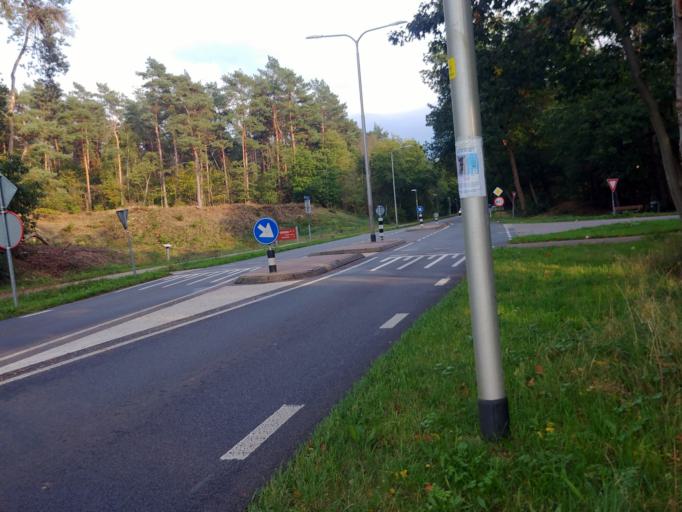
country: NL
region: Gelderland
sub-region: Gemeente Renkum
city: Renkum
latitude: 51.9897
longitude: 5.7319
